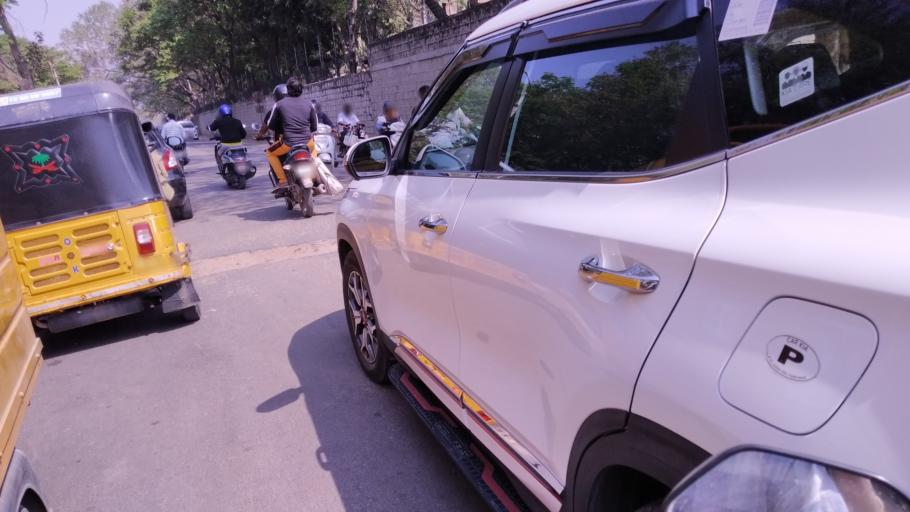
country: IN
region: Telangana
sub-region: Hyderabad
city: Malkajgiri
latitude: 17.4602
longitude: 78.4849
